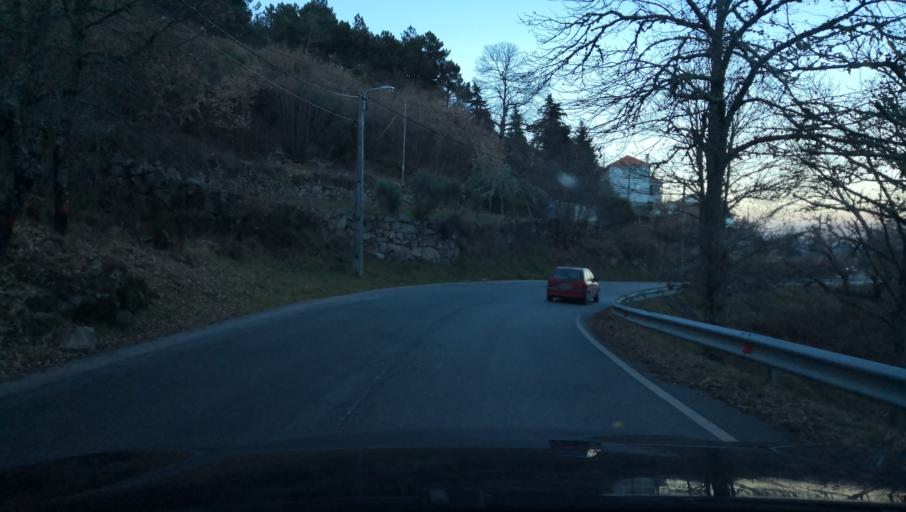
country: PT
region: Vila Real
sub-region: Vila Pouca de Aguiar
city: Vila Pouca de Aguiar
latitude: 41.4926
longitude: -7.6540
